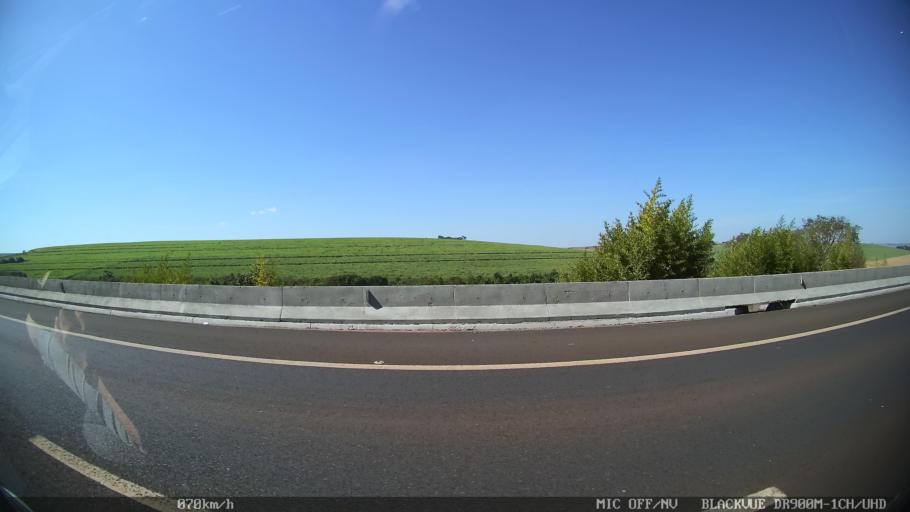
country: BR
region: Sao Paulo
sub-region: Batatais
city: Batatais
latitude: -20.7105
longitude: -47.5047
